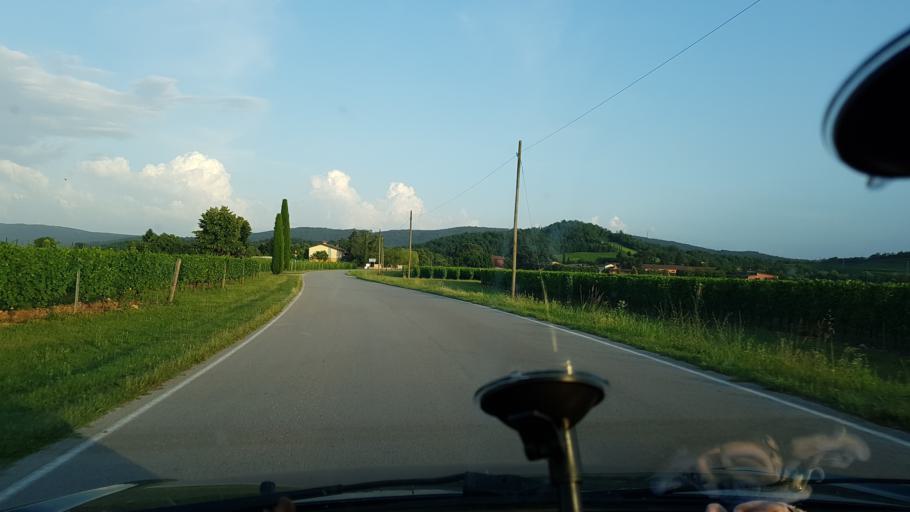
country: IT
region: Friuli Venezia Giulia
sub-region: Provincia di Gorizia
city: San Lorenzo Isontino
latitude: 45.9184
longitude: 13.5313
